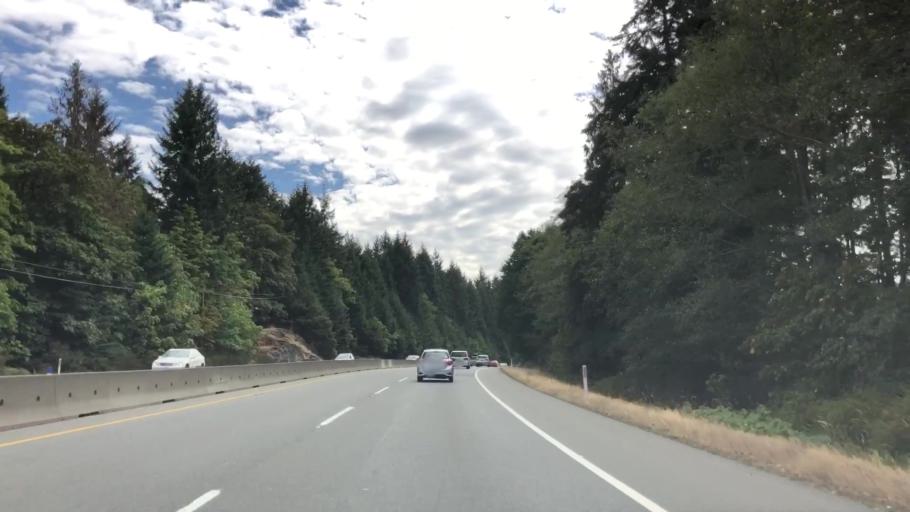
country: CA
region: British Columbia
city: North Cowichan
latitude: 48.8448
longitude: -123.7189
